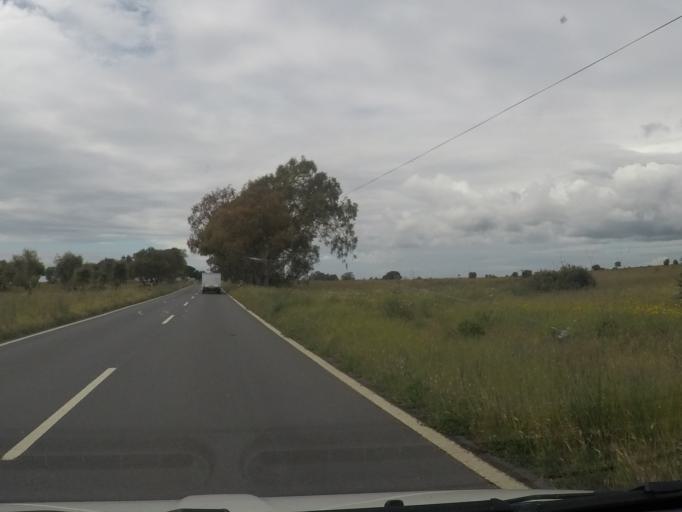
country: PT
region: Setubal
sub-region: Sines
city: Porto Covo
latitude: 37.8857
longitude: -8.7531
